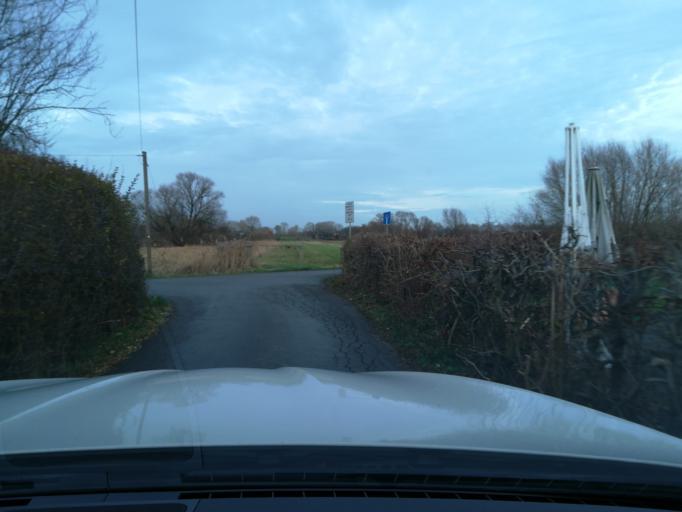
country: DE
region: Hamburg
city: Harburg
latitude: 53.4637
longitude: 10.0127
